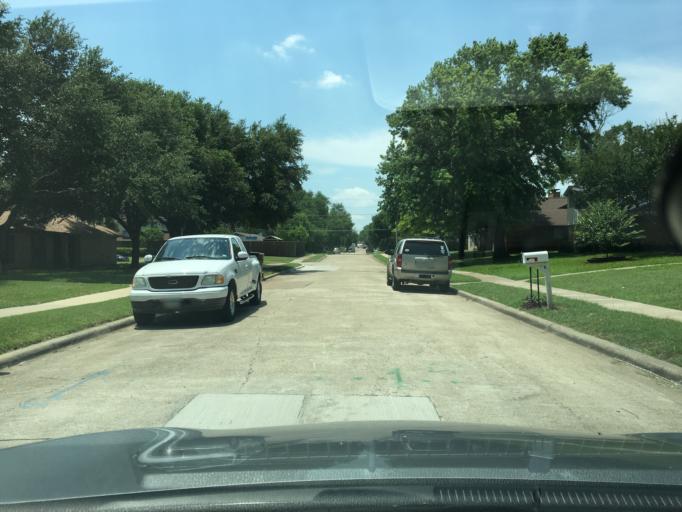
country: US
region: Texas
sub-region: Dallas County
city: Richardson
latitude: 32.9644
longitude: -96.6865
